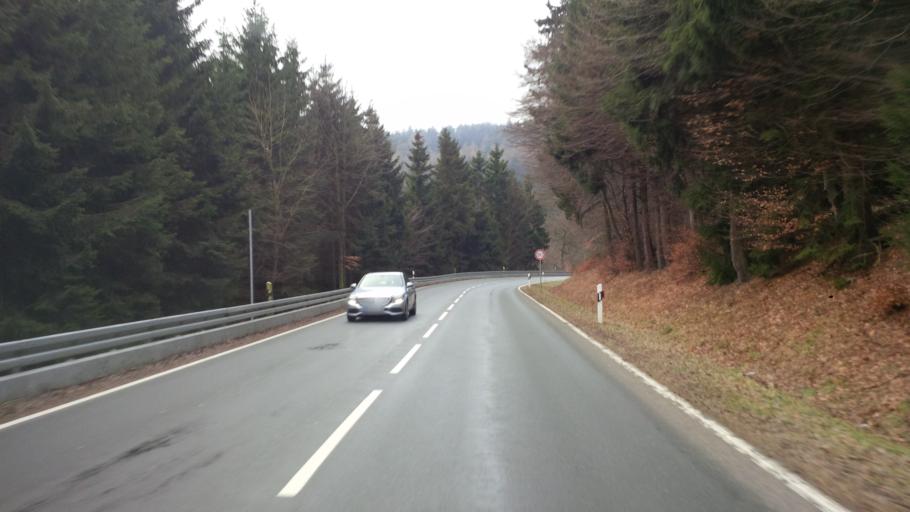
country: DE
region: Hesse
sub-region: Regierungsbezirk Darmstadt
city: Schmitten
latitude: 50.2382
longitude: 8.4843
